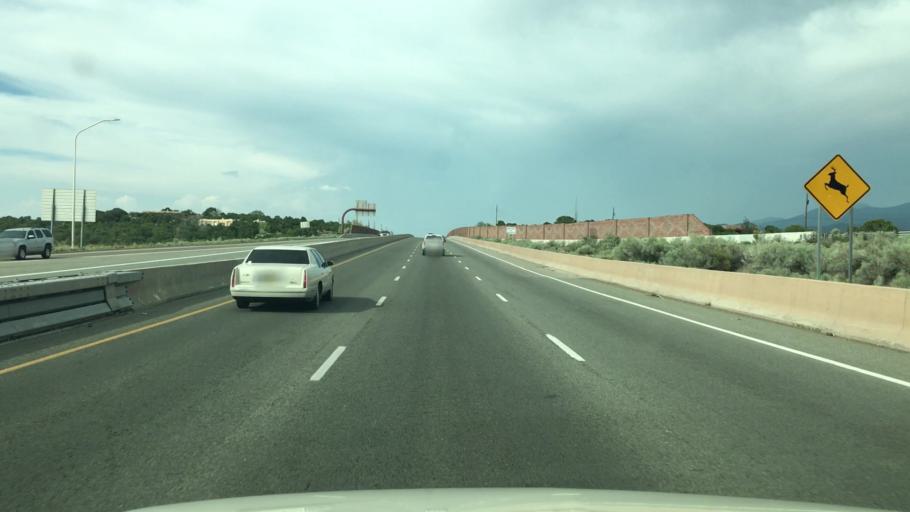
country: US
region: New Mexico
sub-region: Santa Fe County
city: Santa Fe
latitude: 35.7142
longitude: -105.9373
